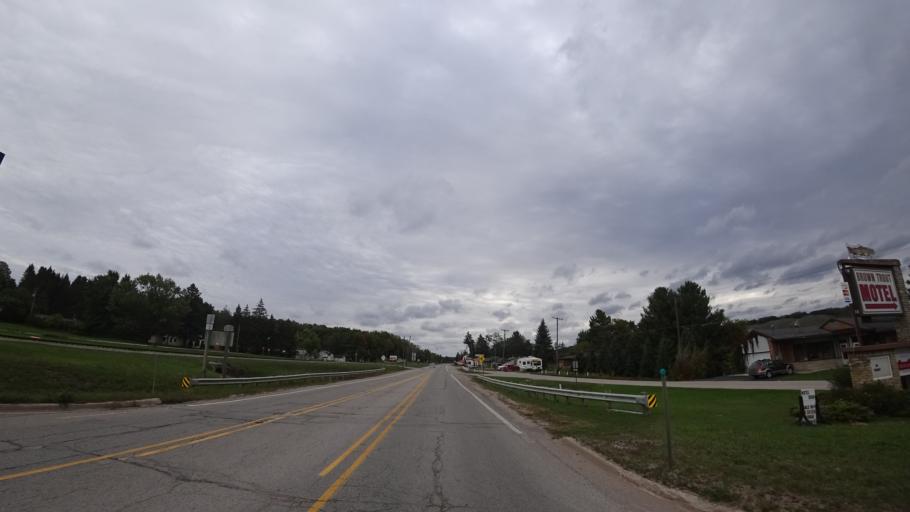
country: US
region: Michigan
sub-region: Charlevoix County
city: Boyne City
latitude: 45.1672
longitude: -84.9169
